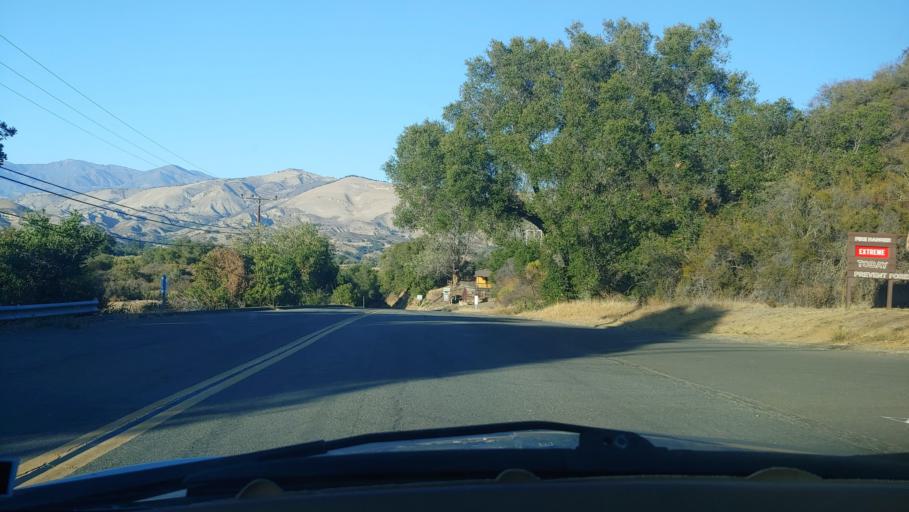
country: US
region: California
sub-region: Santa Barbara County
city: Goleta
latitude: 34.5355
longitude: -119.8519
